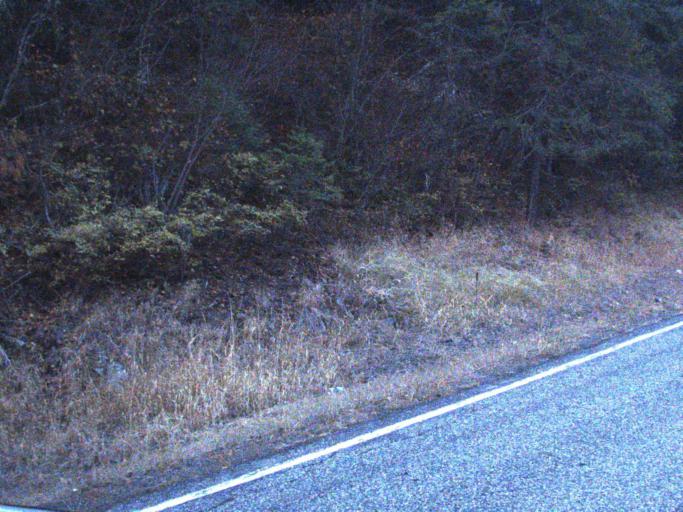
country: US
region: Washington
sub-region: Ferry County
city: Republic
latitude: 48.4274
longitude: -118.7278
